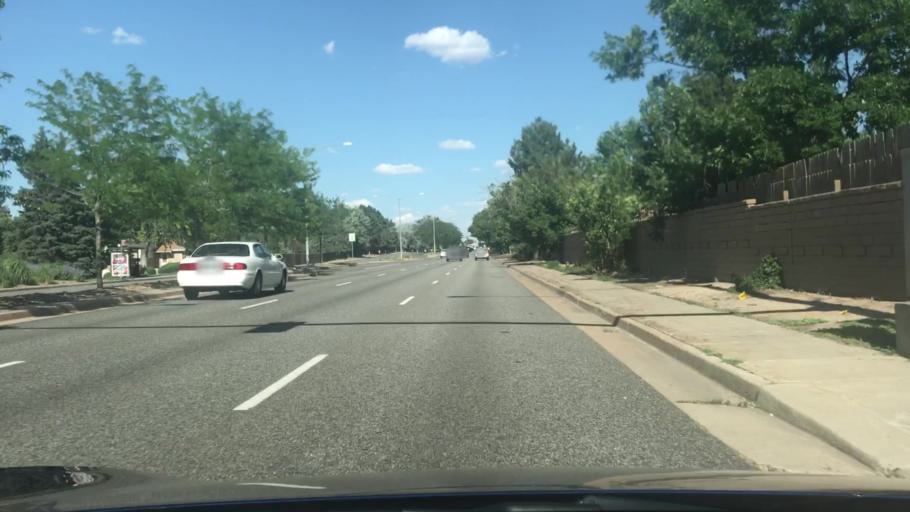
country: US
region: Colorado
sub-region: Arapahoe County
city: Dove Valley
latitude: 39.6530
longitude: -104.7975
